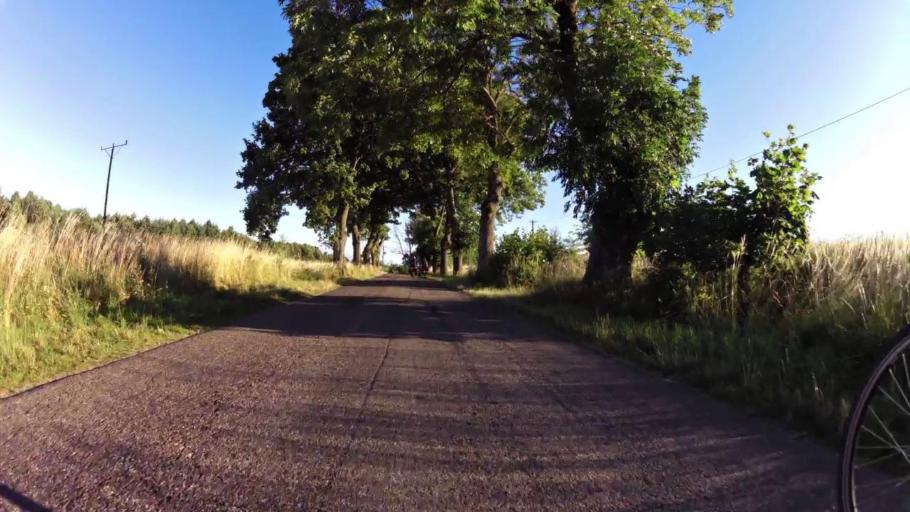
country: PL
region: West Pomeranian Voivodeship
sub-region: Powiat swidwinski
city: Swidwin
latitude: 53.7451
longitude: 15.6880
